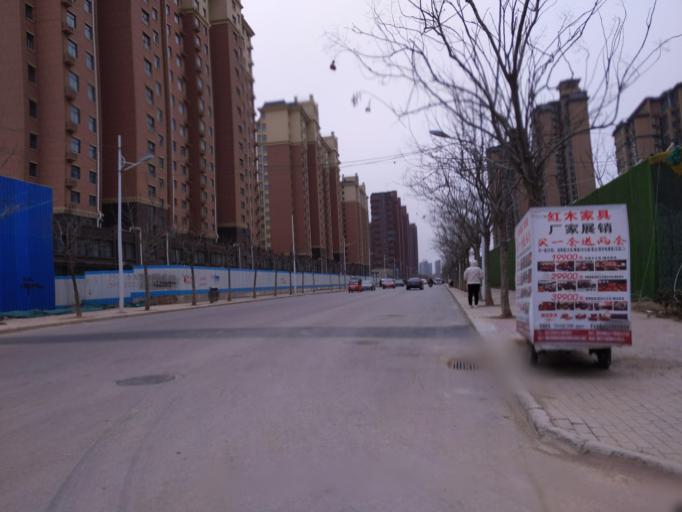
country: CN
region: Henan Sheng
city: Zhongyuanlu
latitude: 35.7428
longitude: 115.0742
